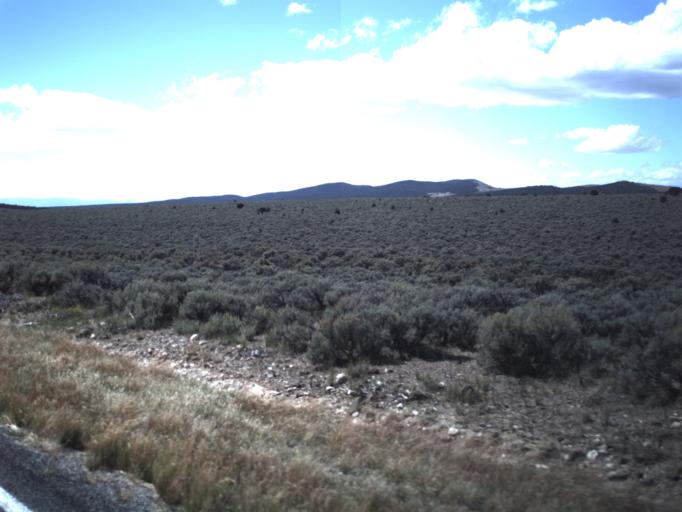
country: US
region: Utah
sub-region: Iron County
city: Parowan
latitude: 38.0608
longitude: -112.9662
